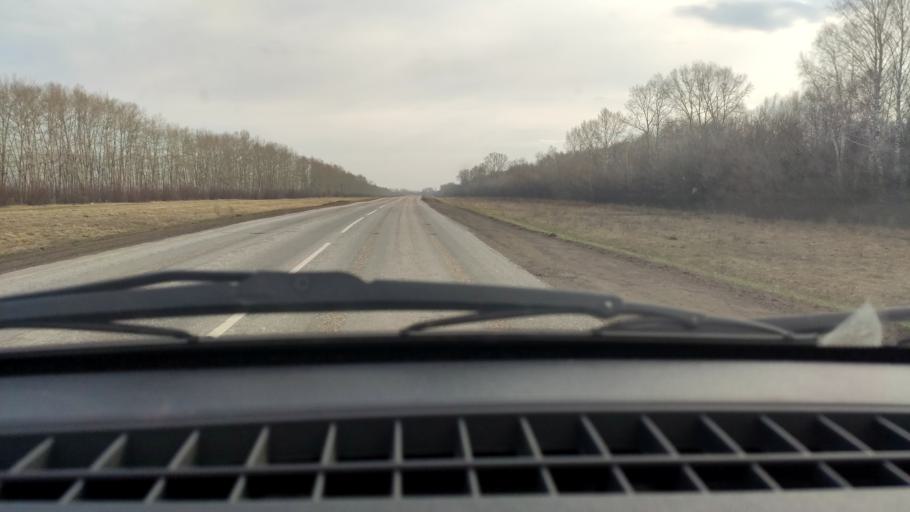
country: RU
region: Bashkortostan
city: Davlekanovo
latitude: 54.3516
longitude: 55.1807
